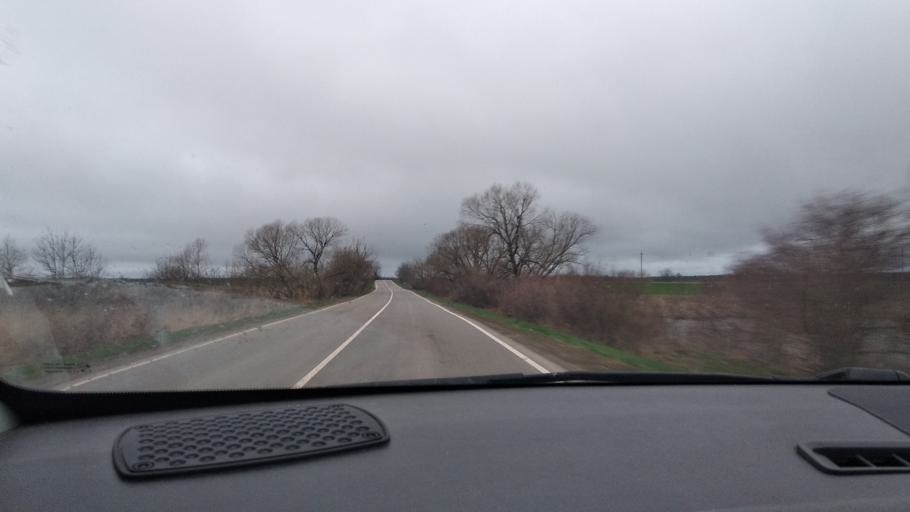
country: RU
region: Krasnodarskiy
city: Afipskiy
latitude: 44.8997
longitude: 38.7925
